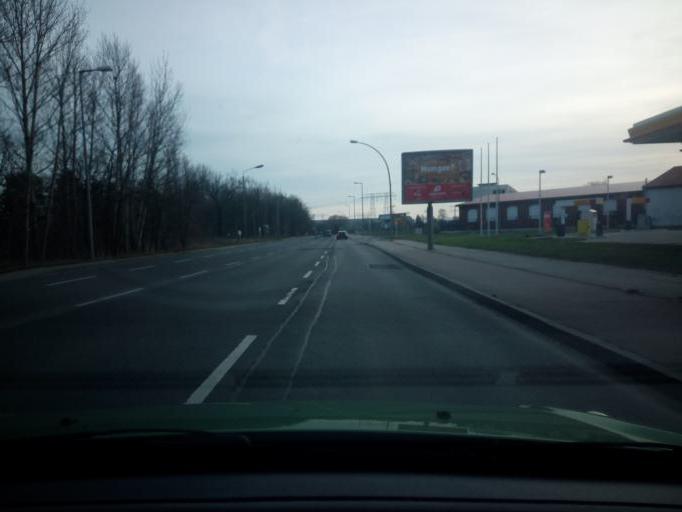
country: DE
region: Berlin
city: Rummelsburg
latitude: 52.4812
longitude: 13.5025
